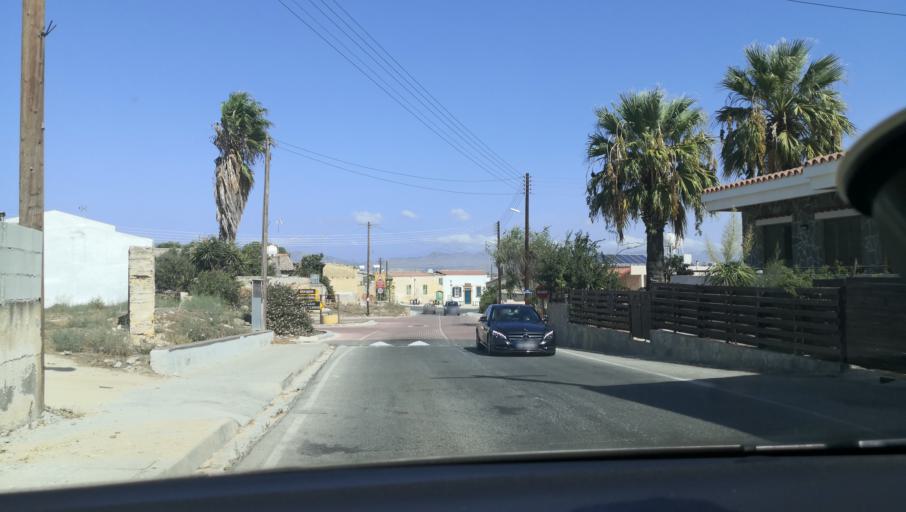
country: CY
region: Lefkosia
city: Mammari
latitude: 35.1730
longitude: 33.2029
